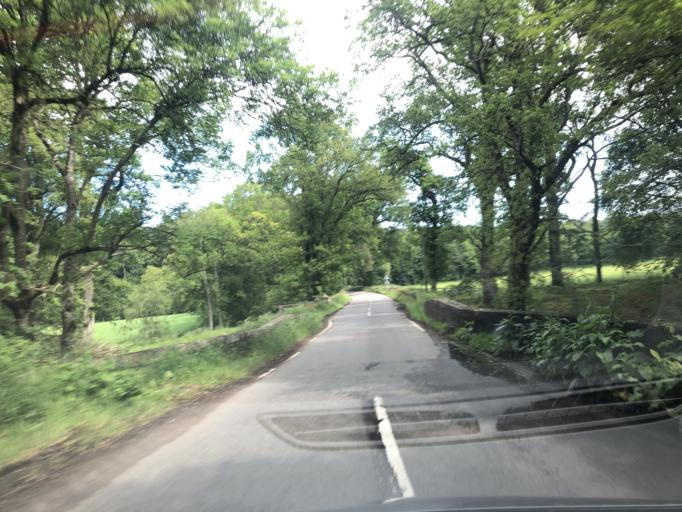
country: GB
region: Scotland
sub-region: Angus
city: Kirriemuir
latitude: 56.7150
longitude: -2.9902
